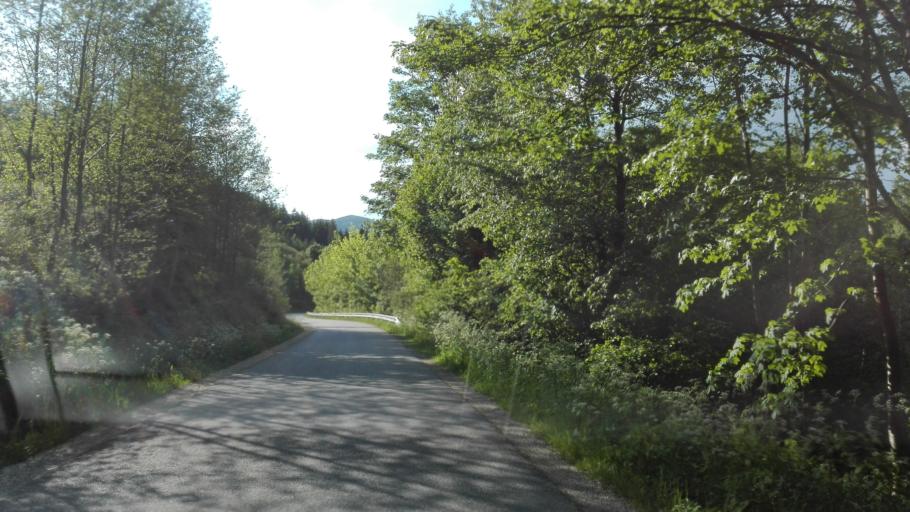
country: AT
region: Upper Austria
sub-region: Politischer Bezirk Perg
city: Perg
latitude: 48.4132
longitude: 14.6617
